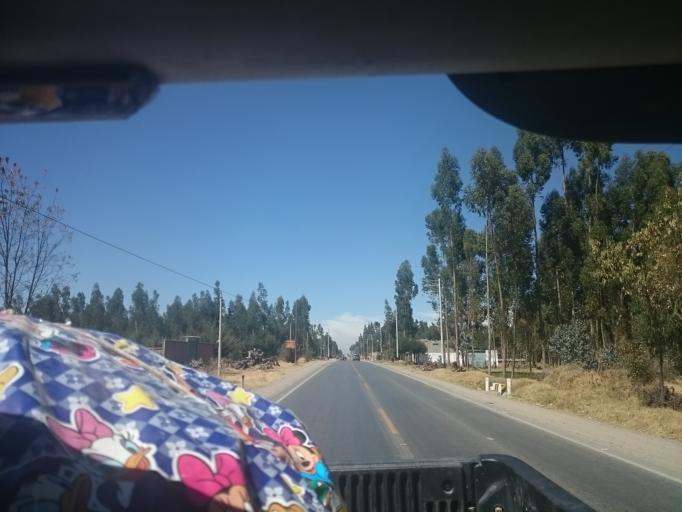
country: PE
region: Junin
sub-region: Provincia de Concepcion
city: Matahuasi
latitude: -11.9008
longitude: -75.3360
